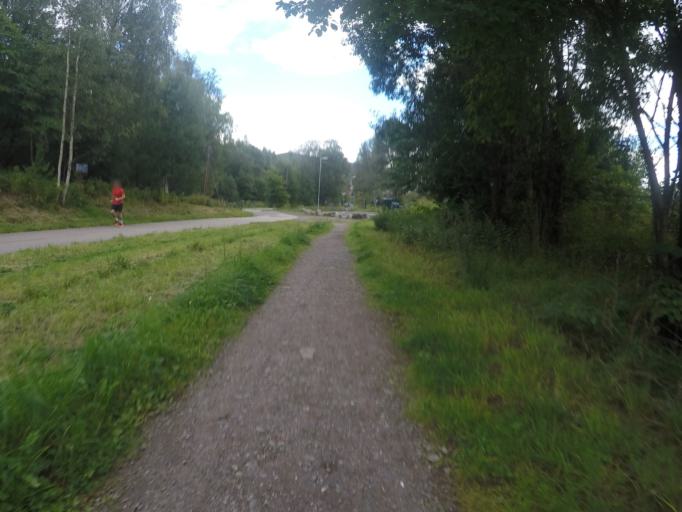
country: NO
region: Oslo
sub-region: Oslo
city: Oslo
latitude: 59.9696
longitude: 10.7746
